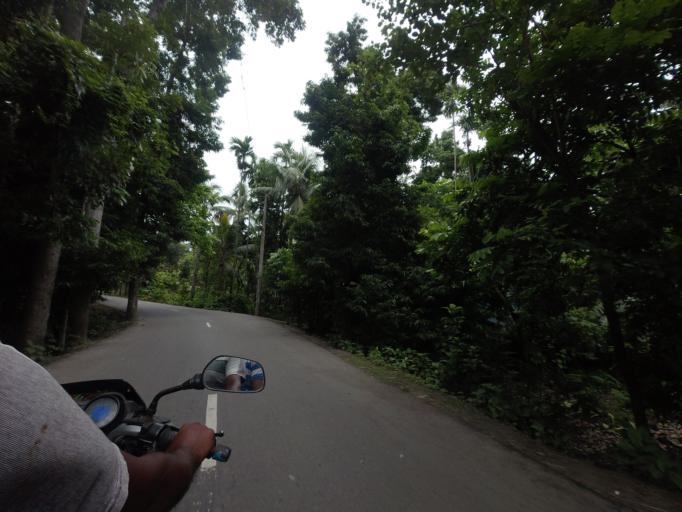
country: BD
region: Khulna
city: Kalia
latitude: 23.1713
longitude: 89.6462
